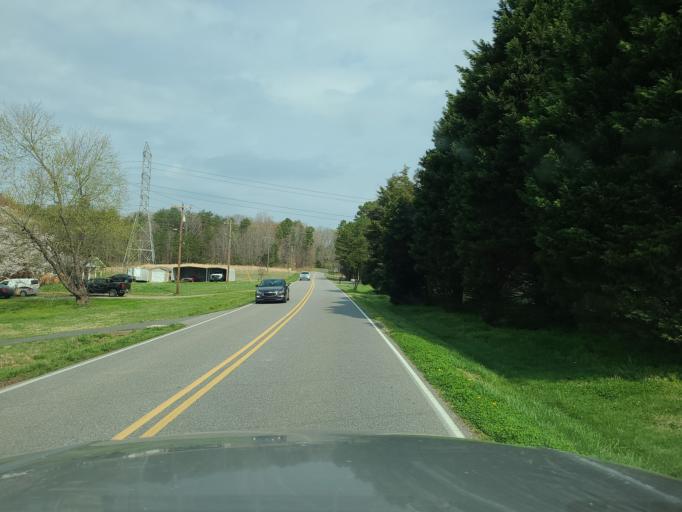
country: US
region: North Carolina
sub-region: Gaston County
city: Ranlo
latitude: 35.3161
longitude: -81.1056
